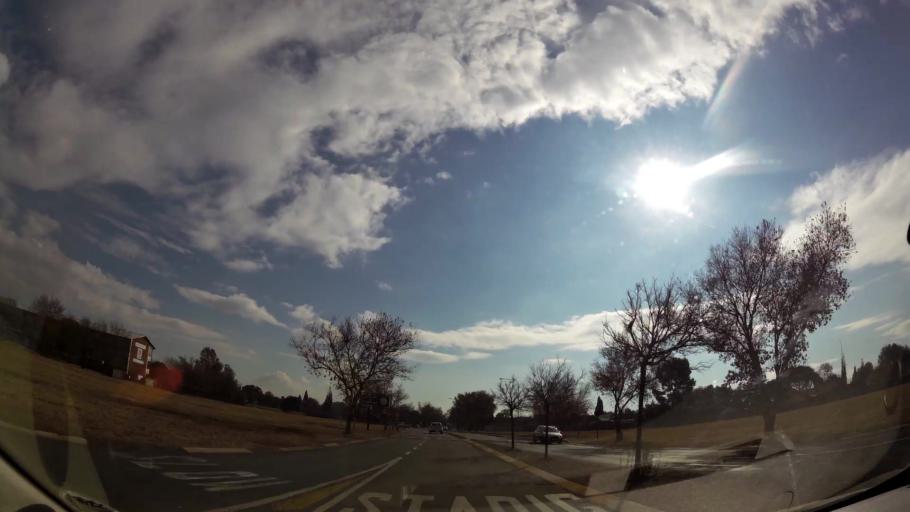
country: ZA
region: Gauteng
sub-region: Sedibeng District Municipality
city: Meyerton
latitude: -26.5563
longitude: 28.0319
